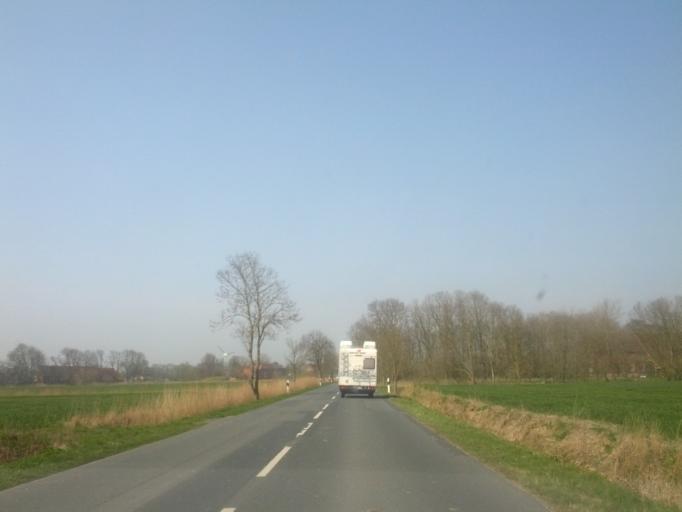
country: DE
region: Lower Saxony
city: Dornum
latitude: 53.6686
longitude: 7.3629
